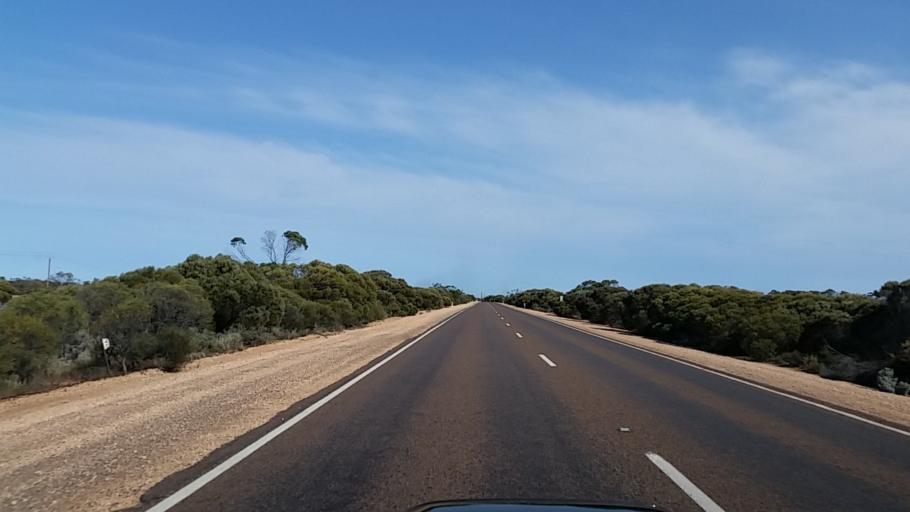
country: AU
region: South Australia
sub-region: Whyalla
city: Whyalla
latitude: -32.9495
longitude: 137.5742
